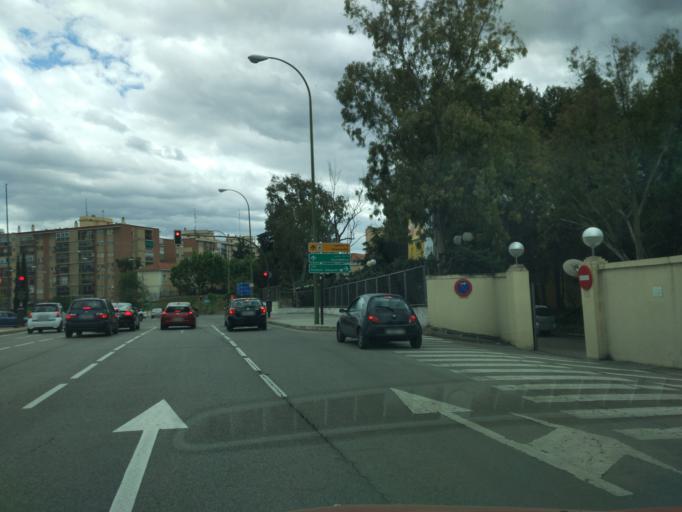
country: ES
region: Madrid
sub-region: Provincia de Madrid
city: Chamartin
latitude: 40.4756
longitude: -3.6900
